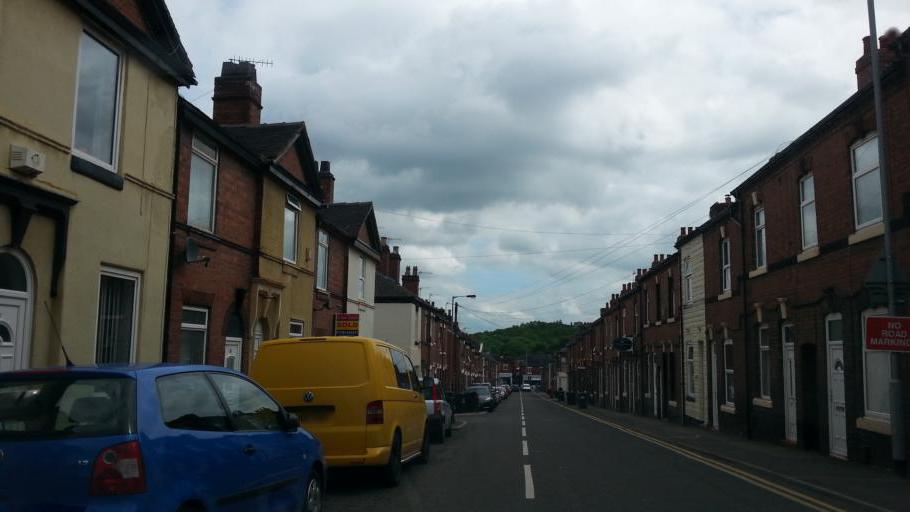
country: GB
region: England
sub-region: Staffordshire
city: Newcastle under Lyme
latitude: 53.0407
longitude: -2.2532
